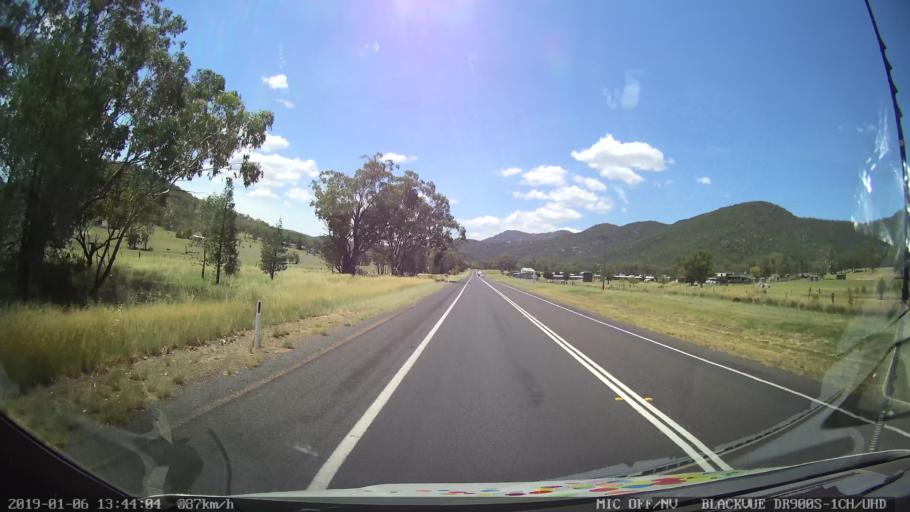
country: AU
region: New South Wales
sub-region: Tamworth Municipality
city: Kootingal
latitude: -31.0103
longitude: 151.0872
